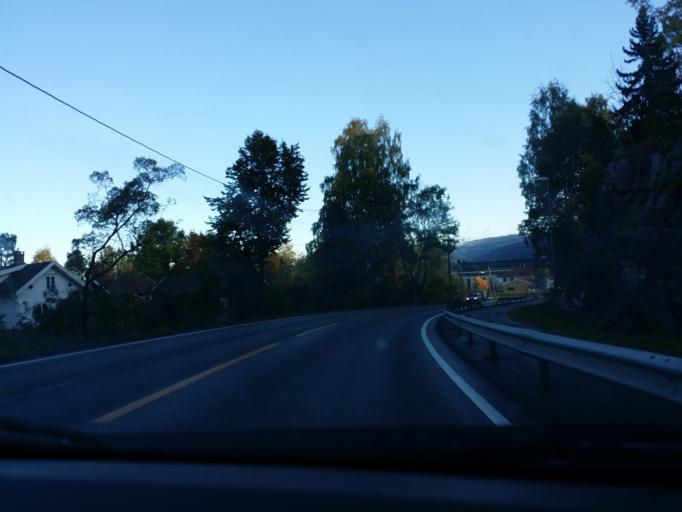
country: NO
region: Buskerud
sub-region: Hole
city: Vik
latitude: 60.0601
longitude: 10.3070
